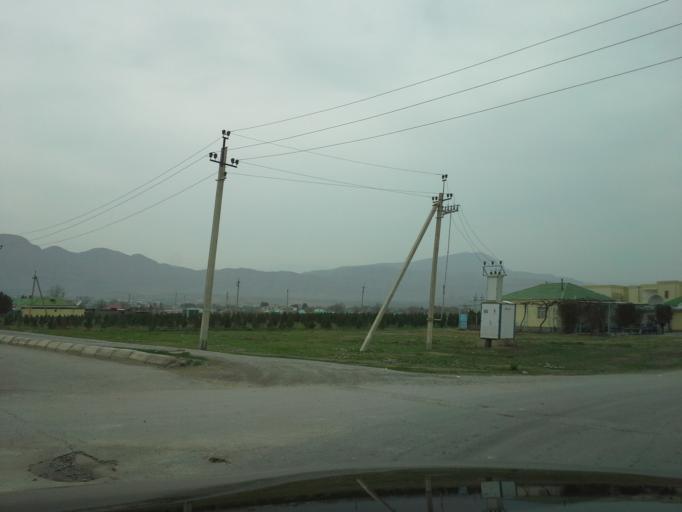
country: TM
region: Ahal
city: Abadan
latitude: 37.9679
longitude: 58.2293
